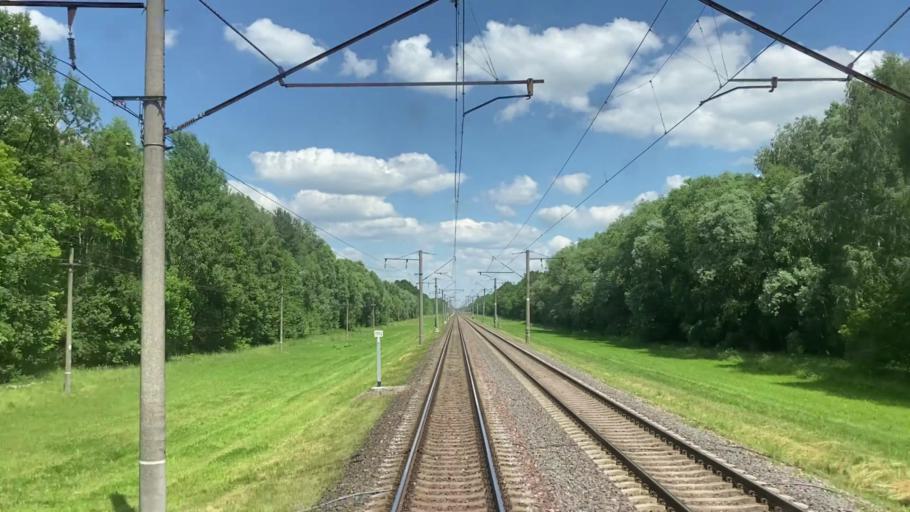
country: BY
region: Brest
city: Zhabinka
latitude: 52.2424
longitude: 24.1023
